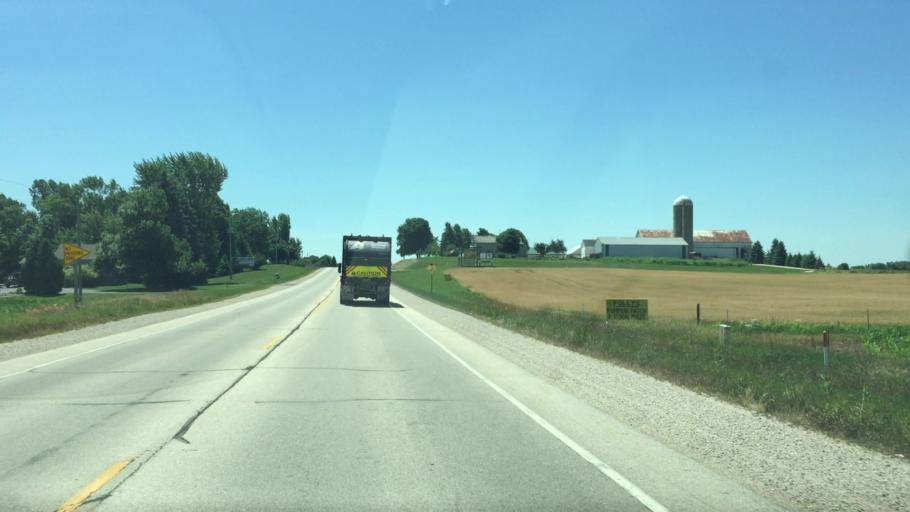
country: US
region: Wisconsin
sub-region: Calumet County
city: Chilton
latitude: 44.0495
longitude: -88.1630
